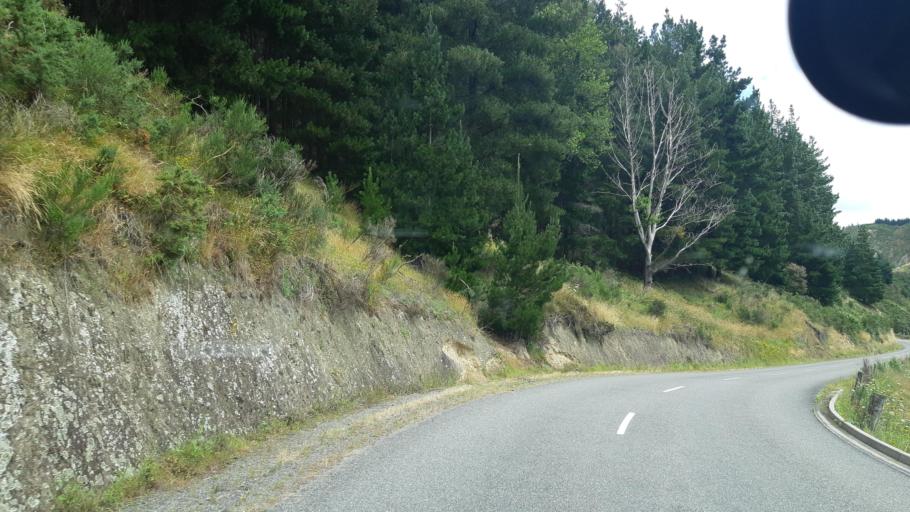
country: NZ
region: Marlborough
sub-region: Marlborough District
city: Blenheim
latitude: -41.4865
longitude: 173.7516
